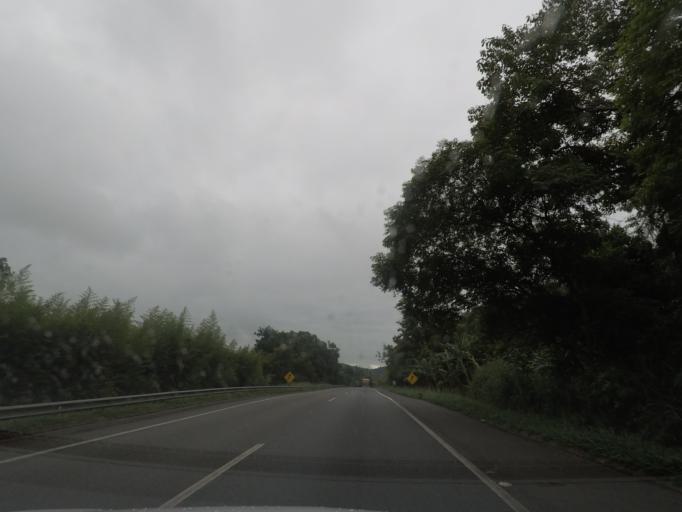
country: BR
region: Sao Paulo
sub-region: Cajati
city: Cajati
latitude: -24.7943
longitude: -48.2078
